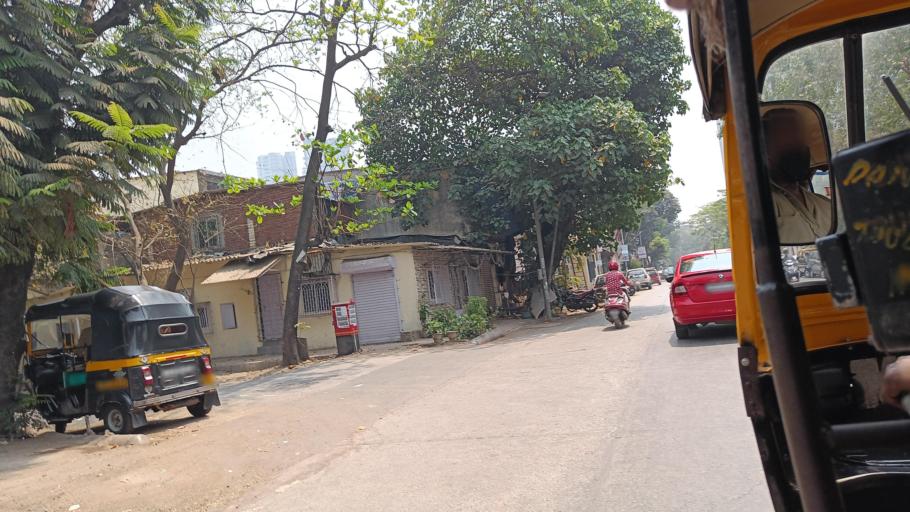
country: IN
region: Maharashtra
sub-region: Mumbai Suburban
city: Powai
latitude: 19.1548
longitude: 72.8374
